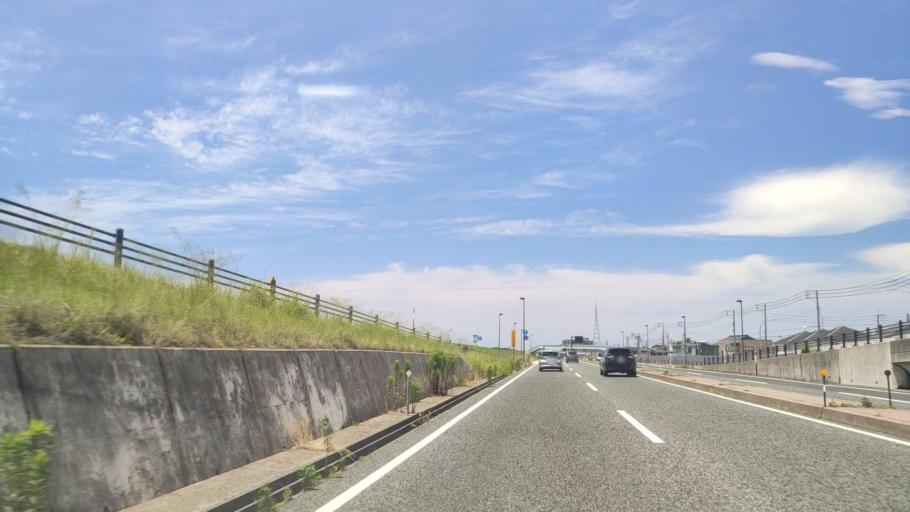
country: JP
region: Tottori
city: Tottori
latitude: 35.5056
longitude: 134.2170
